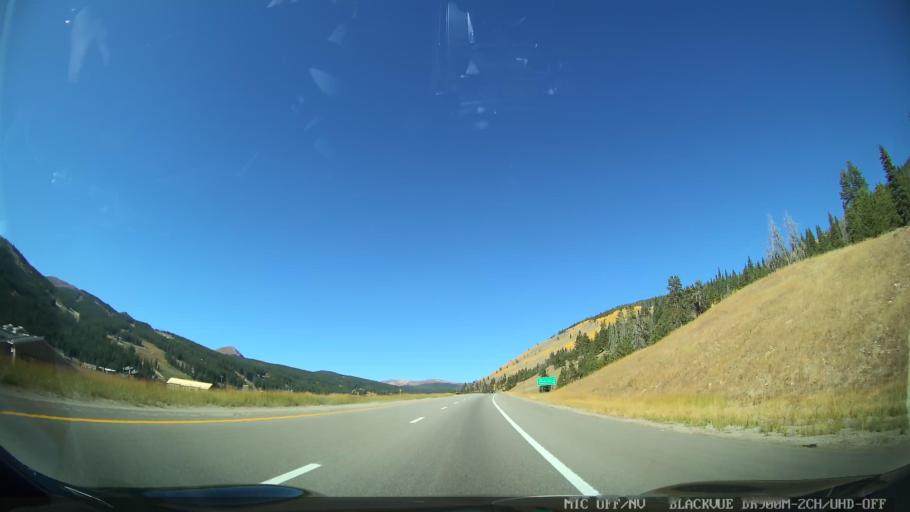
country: US
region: Colorado
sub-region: Summit County
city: Frisco
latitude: 39.5037
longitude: -106.1486
